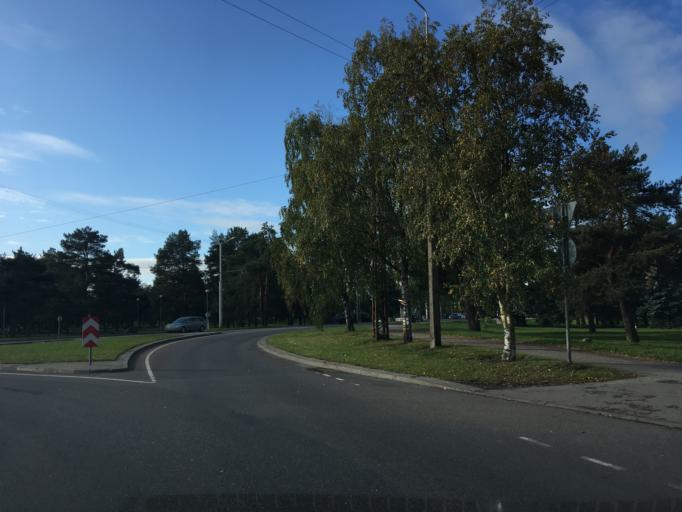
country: EE
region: Harju
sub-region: Saue vald
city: Laagri
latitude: 59.4010
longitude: 24.6770
